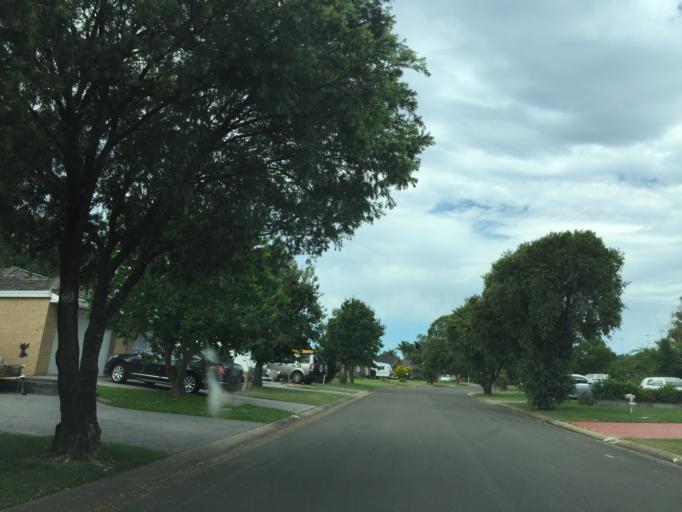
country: AU
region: New South Wales
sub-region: Blacktown
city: Mount Druitt
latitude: -33.8028
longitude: 150.7875
